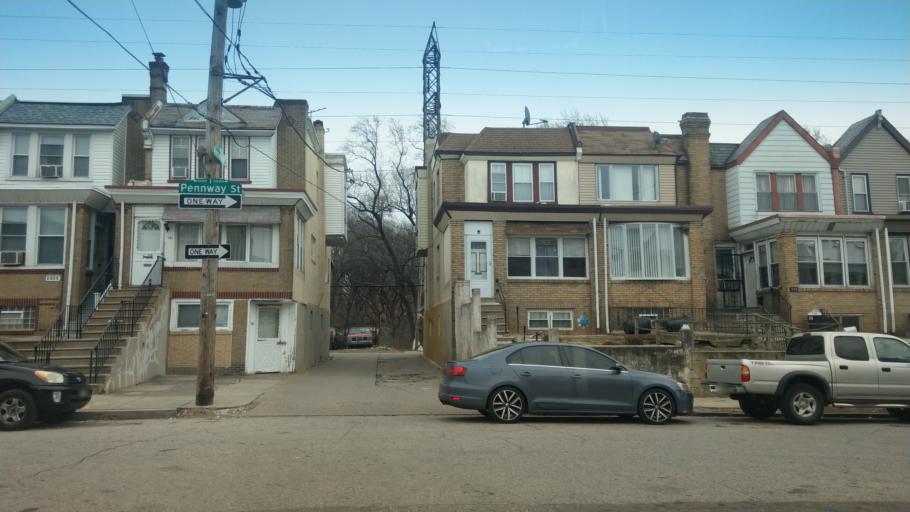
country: US
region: Pennsylvania
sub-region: Montgomery County
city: Rockledge
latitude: 40.0261
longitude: -75.1073
